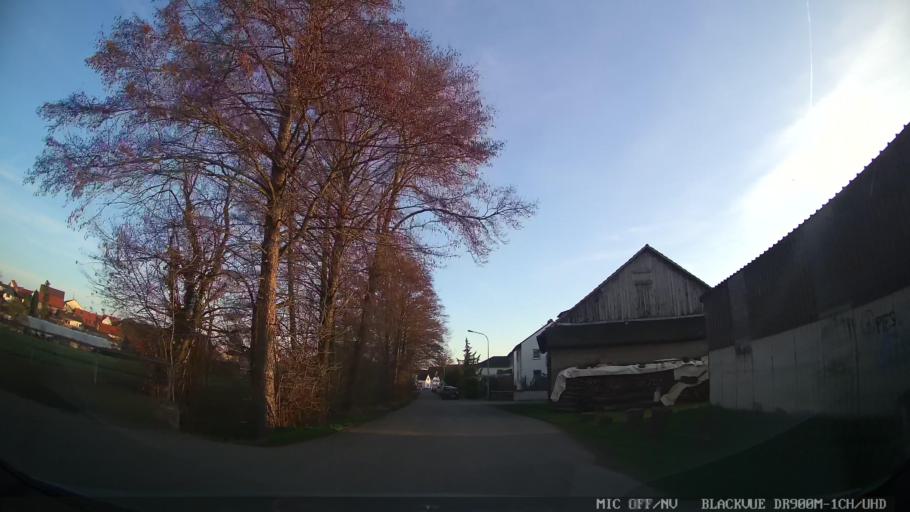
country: DE
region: Hesse
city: Dieburg
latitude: 49.8755
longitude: 8.8858
